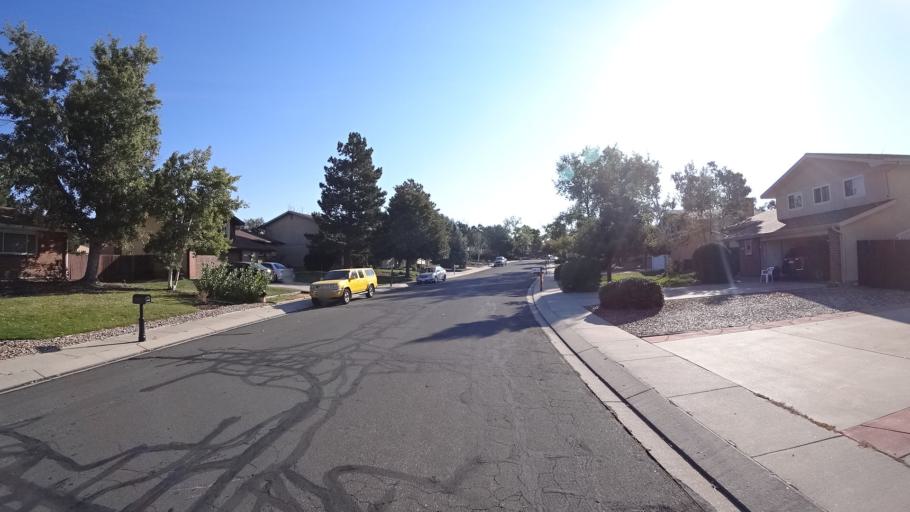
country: US
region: Colorado
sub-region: El Paso County
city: Cimarron Hills
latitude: 38.8876
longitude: -104.7301
